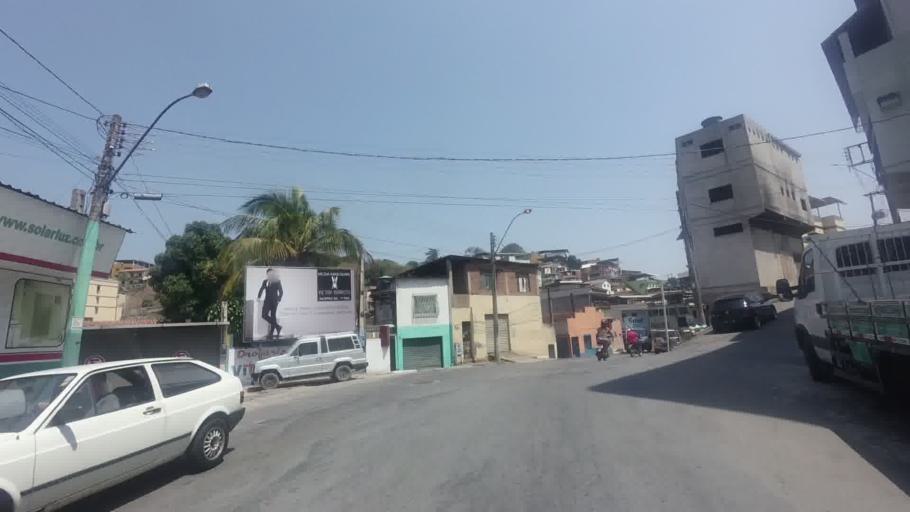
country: BR
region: Espirito Santo
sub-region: Cachoeiro De Itapemirim
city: Cachoeiro de Itapemirim
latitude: -20.8411
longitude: -41.1239
